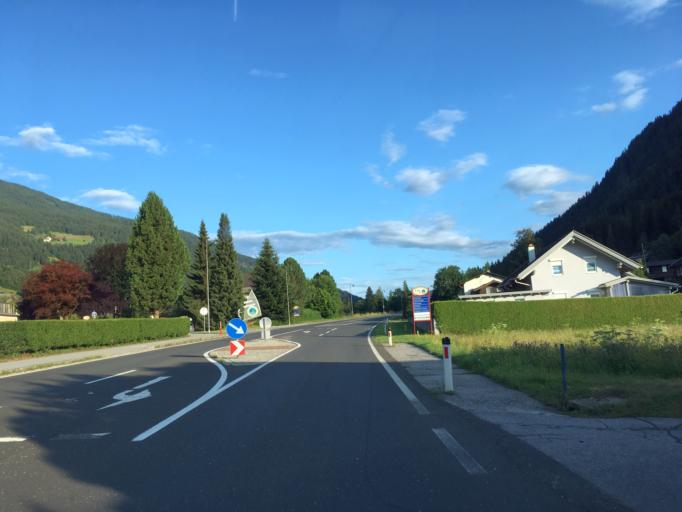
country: AT
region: Carinthia
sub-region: Politischer Bezirk Villach Land
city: Feld am See
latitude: 46.7795
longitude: 13.7422
